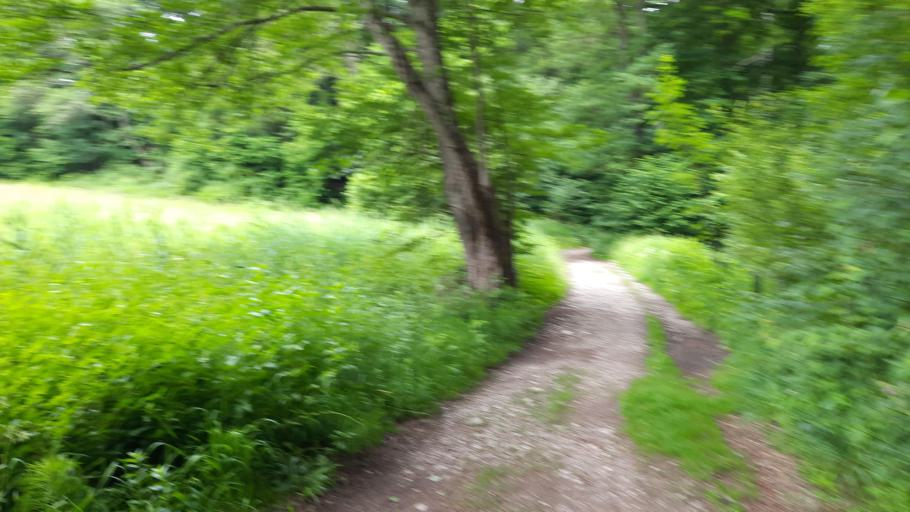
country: DE
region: Bavaria
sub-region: Upper Bavaria
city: Vagen
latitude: 47.8435
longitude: 11.8608
